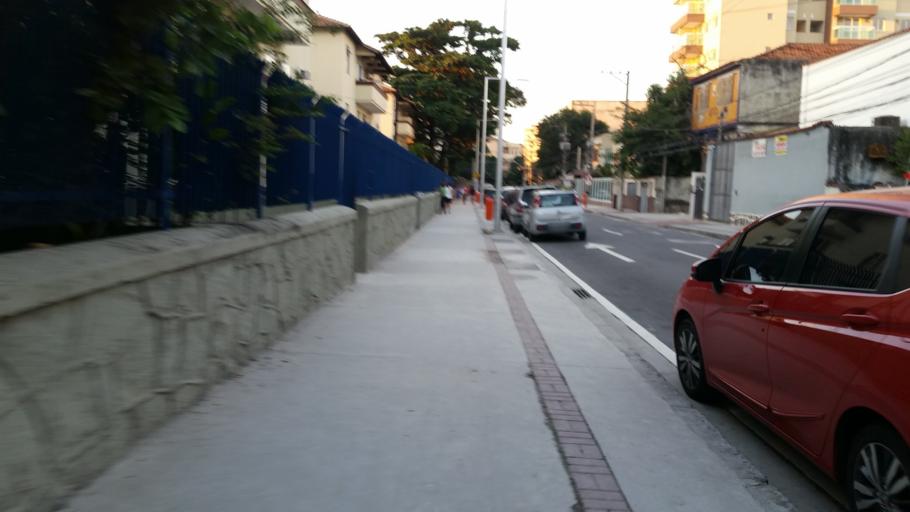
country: BR
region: Rio de Janeiro
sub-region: Rio De Janeiro
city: Rio de Janeiro
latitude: -22.8934
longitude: -43.2895
